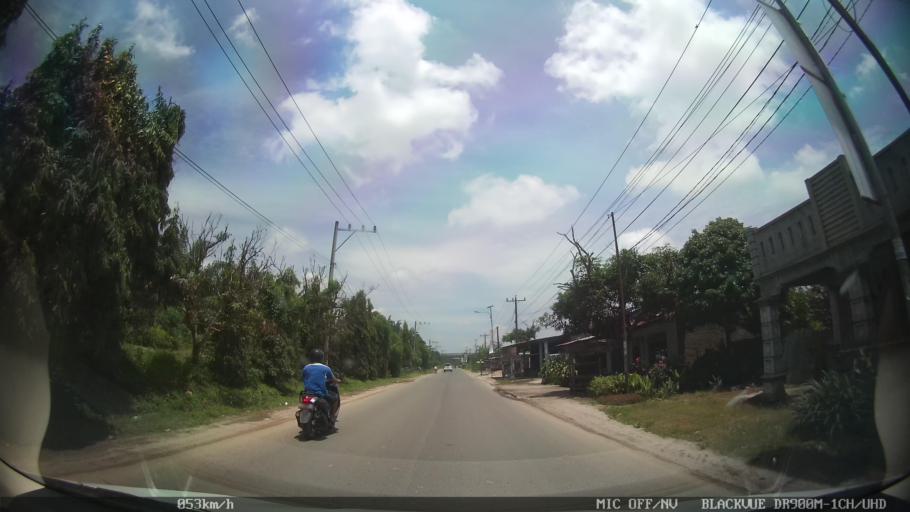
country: ID
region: North Sumatra
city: Perbaungan
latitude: 3.5282
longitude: 98.8879
